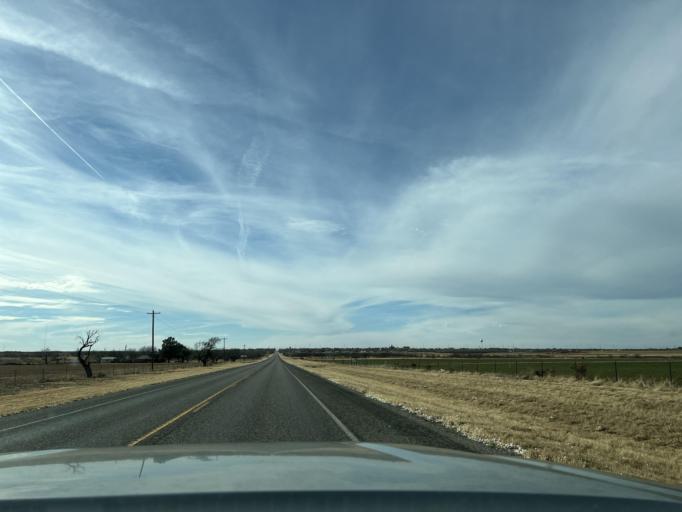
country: US
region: Texas
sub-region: Jones County
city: Anson
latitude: 32.7514
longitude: -99.8705
